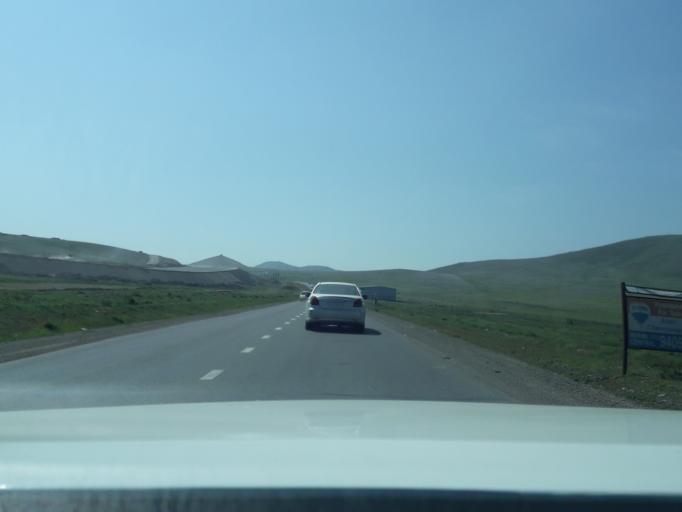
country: MN
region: Ulaanbaatar
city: Ulaanbaatar
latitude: 47.7997
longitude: 106.7463
